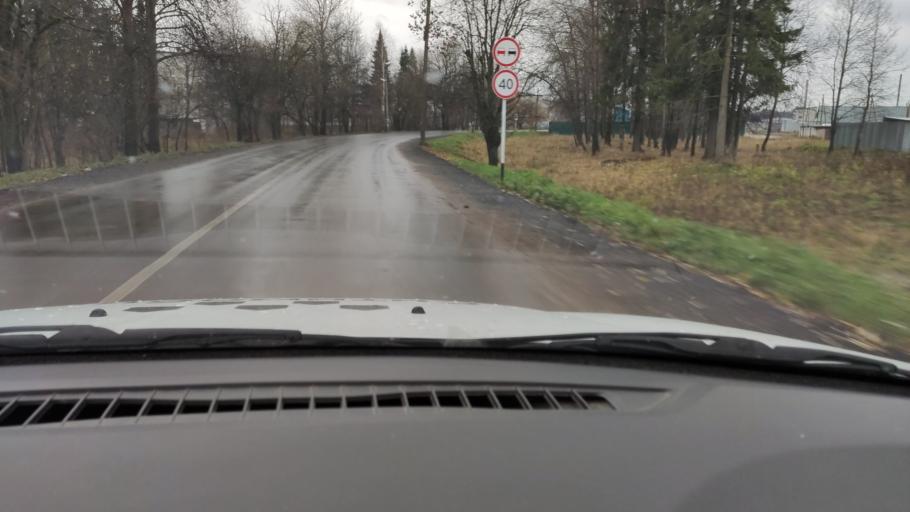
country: RU
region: Perm
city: Sylva
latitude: 58.0323
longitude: 56.7405
